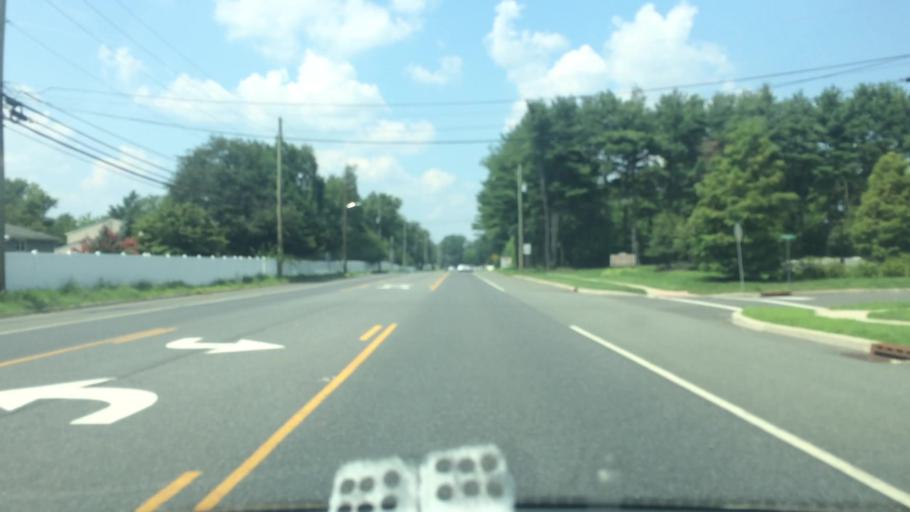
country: US
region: New Jersey
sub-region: Gloucester County
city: Turnersville
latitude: 39.7575
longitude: -75.0814
